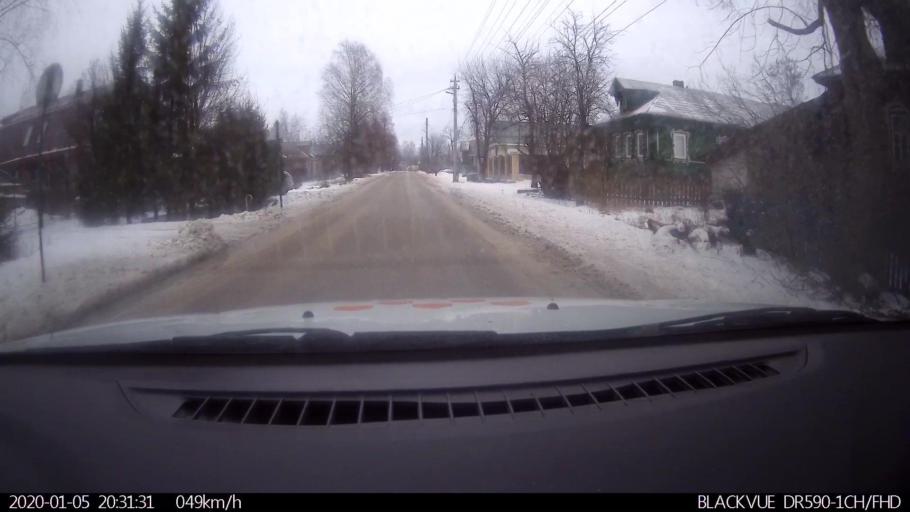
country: RU
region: Nizjnij Novgorod
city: Lukino
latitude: 56.4065
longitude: 43.7287
